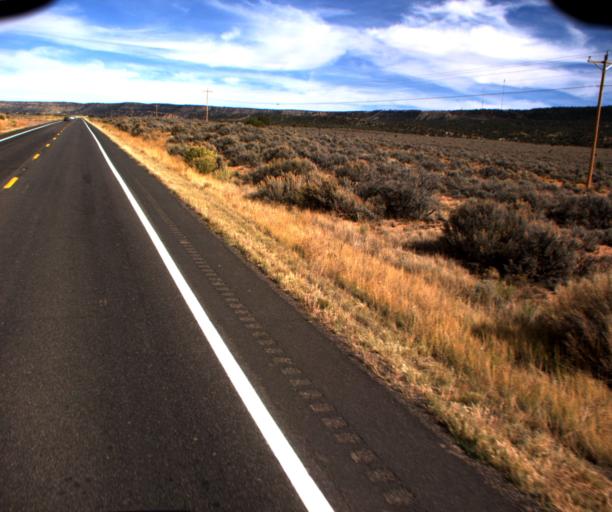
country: US
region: Arizona
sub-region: Navajo County
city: Kayenta
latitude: 36.5490
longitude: -110.5304
